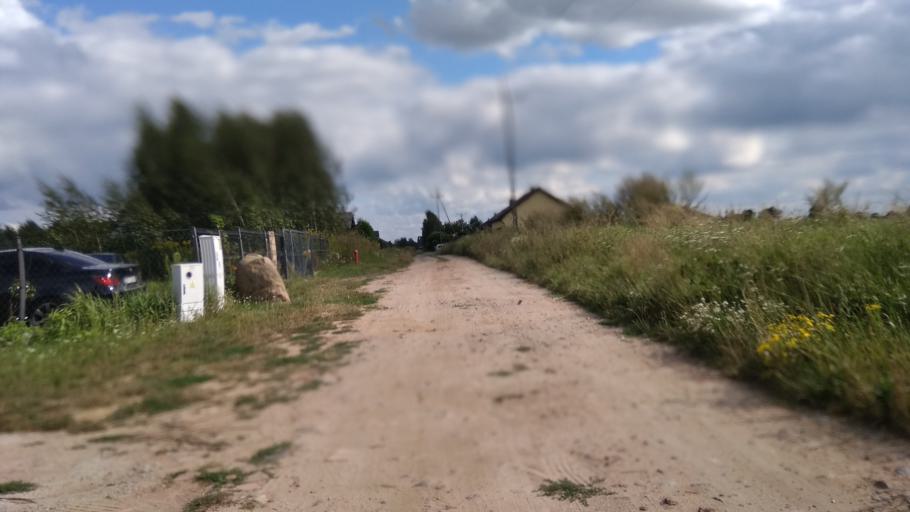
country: PL
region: Kujawsko-Pomorskie
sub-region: Powiat bydgoski
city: Osielsko
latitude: 53.2204
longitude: 18.1443
